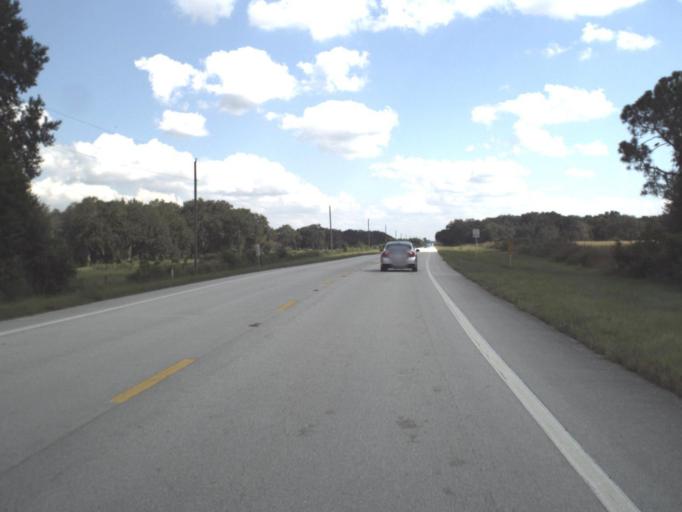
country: US
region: Florida
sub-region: Highlands County
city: Lake Placid
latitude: 27.3805
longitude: -81.1069
